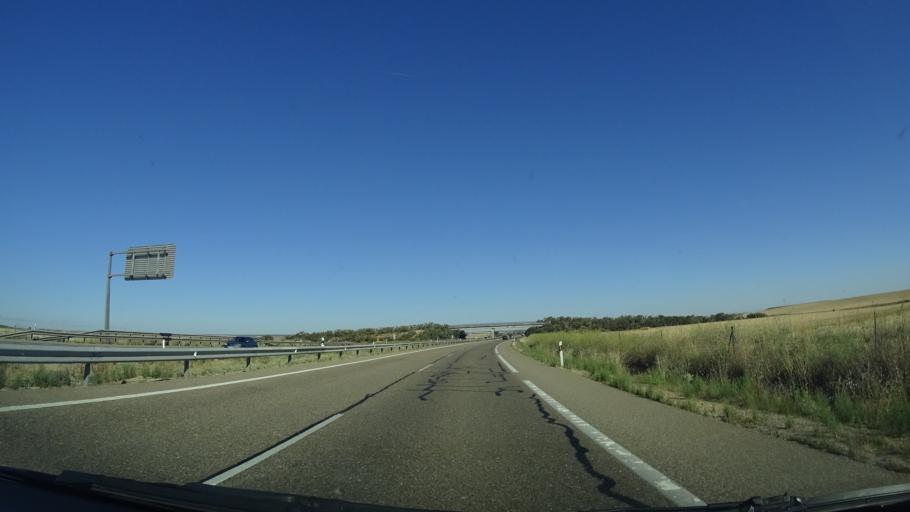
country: ES
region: Castille and Leon
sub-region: Provincia de Valladolid
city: Villardefrades
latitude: 41.7333
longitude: -5.2624
